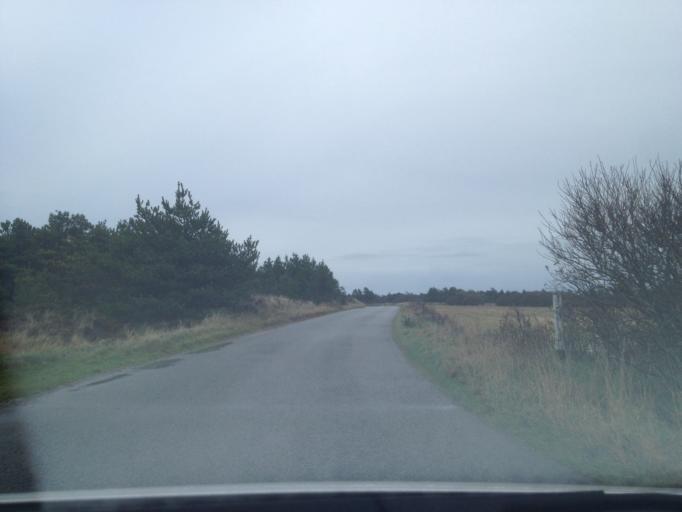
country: DE
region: Schleswig-Holstein
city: List
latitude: 55.1599
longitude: 8.5343
